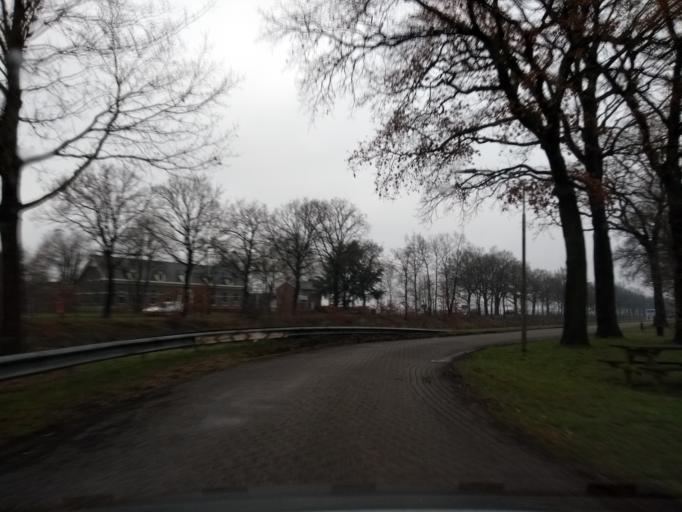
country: NL
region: Drenthe
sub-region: Gemeente Emmen
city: Klazienaveen
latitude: 52.7083
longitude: 6.9446
